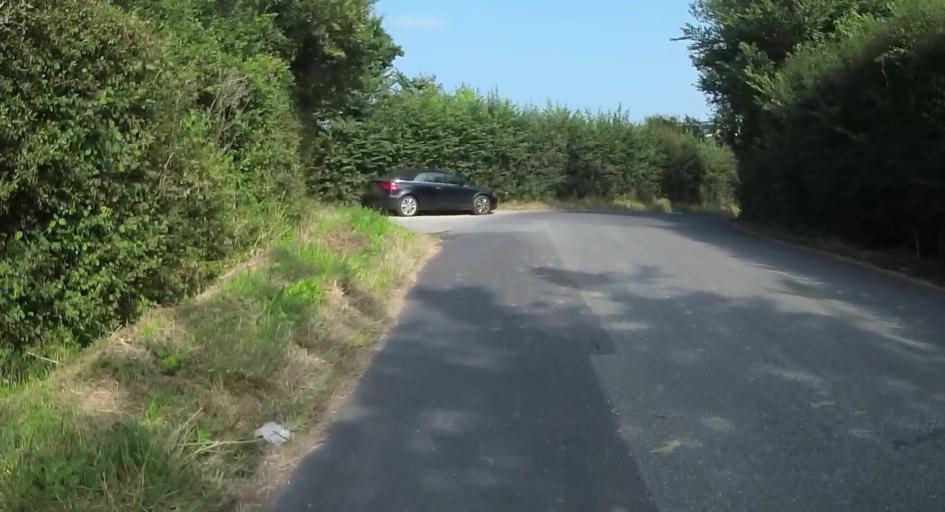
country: GB
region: England
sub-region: Isle of Wight
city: Newport
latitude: 50.7148
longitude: -1.2957
